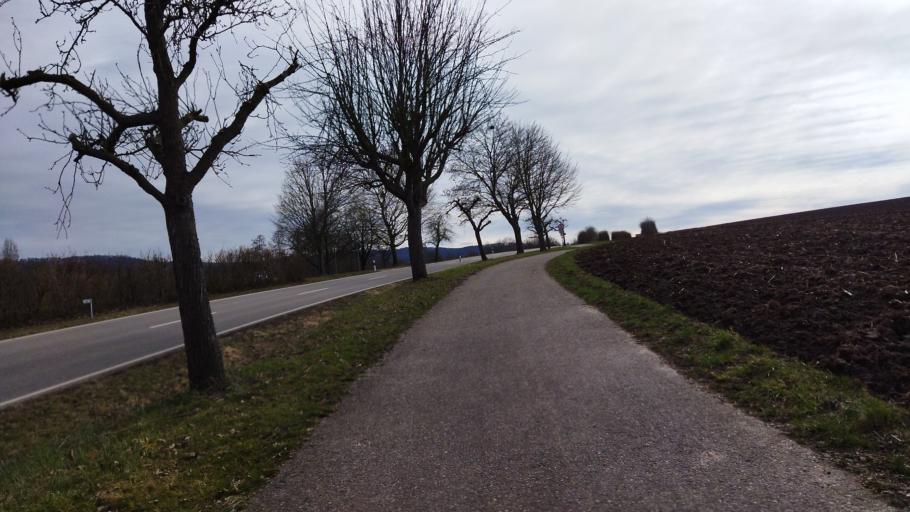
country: DE
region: Baden-Wuerttemberg
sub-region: Regierungsbezirk Stuttgart
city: Lowenstein
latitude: 49.1328
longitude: 9.4016
